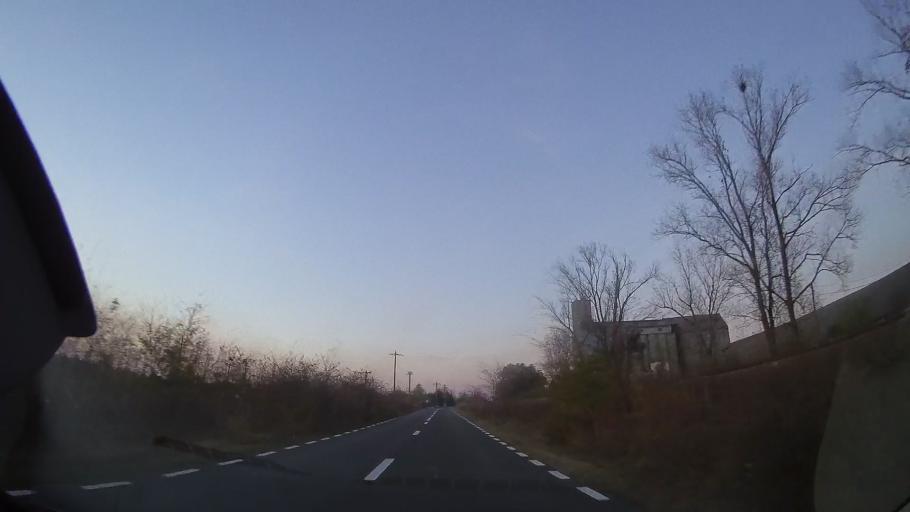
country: RO
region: Constanta
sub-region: Comuna Cobadin
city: Cobadin
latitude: 44.0506
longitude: 28.2488
